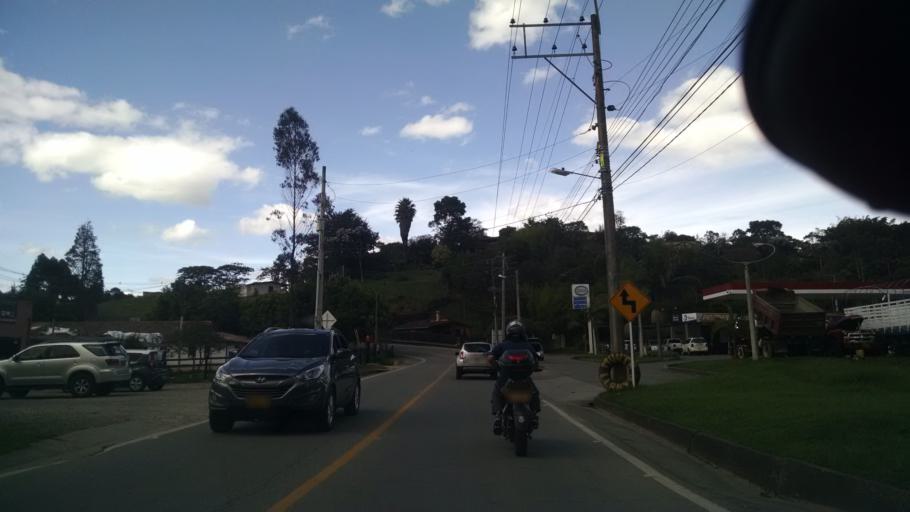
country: CO
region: Antioquia
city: El Retiro
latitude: 6.0743
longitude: -75.4971
